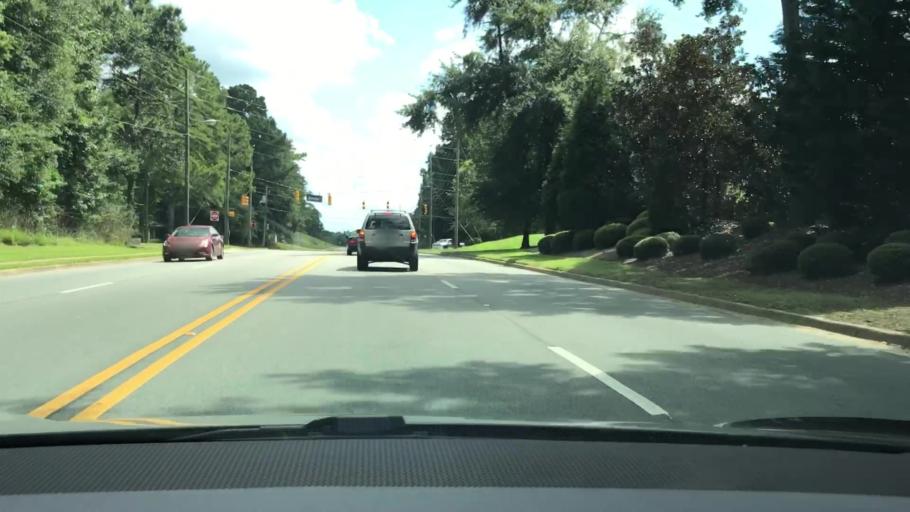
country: US
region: Alabama
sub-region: Lee County
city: Auburn
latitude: 32.6188
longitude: -85.4476
